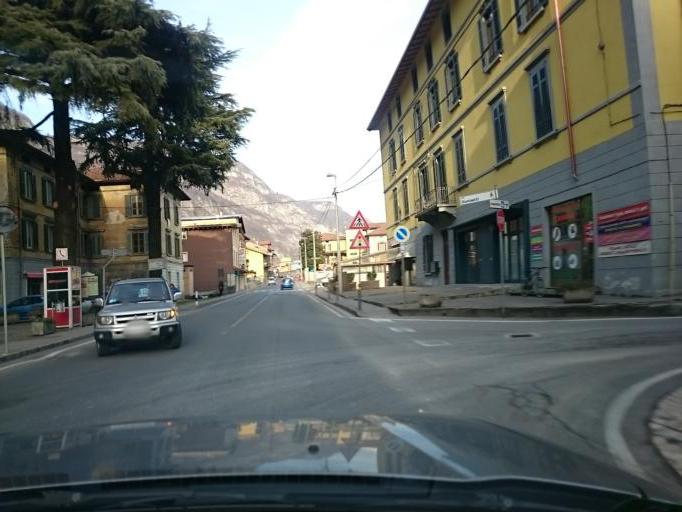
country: IT
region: Lombardy
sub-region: Provincia di Brescia
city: Esine
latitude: 45.9322
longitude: 10.2421
